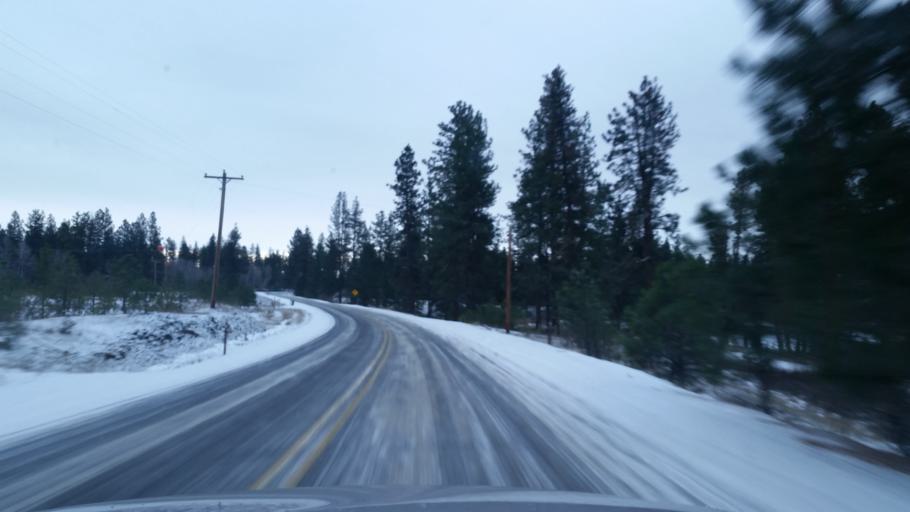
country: US
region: Washington
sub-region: Spokane County
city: Cheney
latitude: 47.4555
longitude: -117.5249
